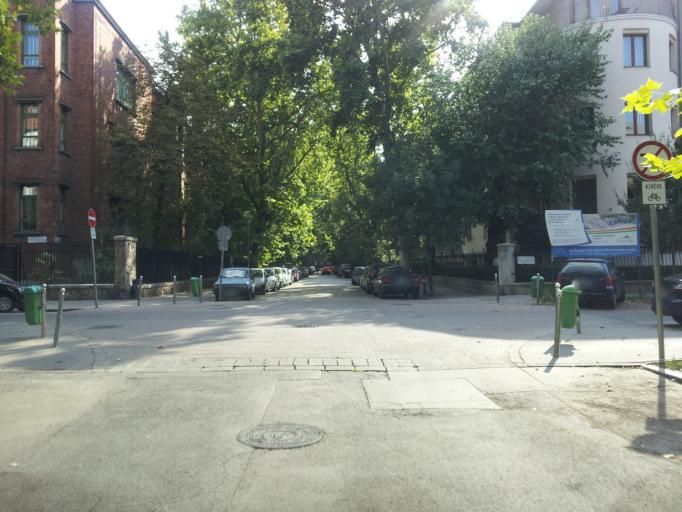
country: HU
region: Budapest
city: Budapest VII. keruelet
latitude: 47.5068
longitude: 19.0892
